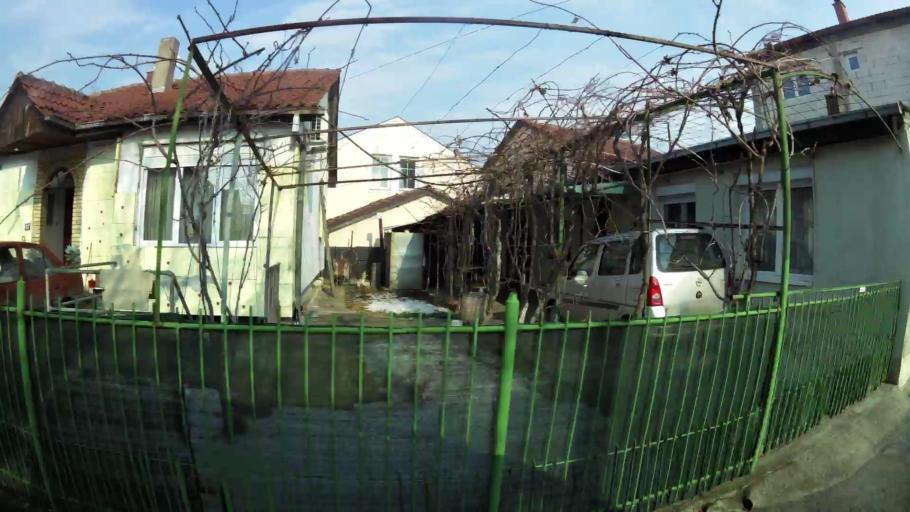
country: MK
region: Kisela Voda
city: Kisela Voda
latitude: 41.9912
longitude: 21.4980
